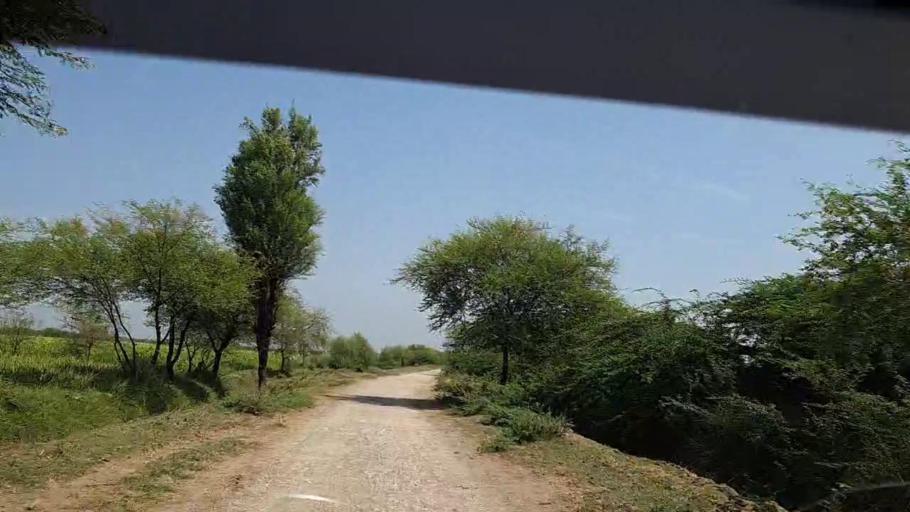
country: PK
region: Sindh
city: Rajo Khanani
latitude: 24.9247
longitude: 68.8667
